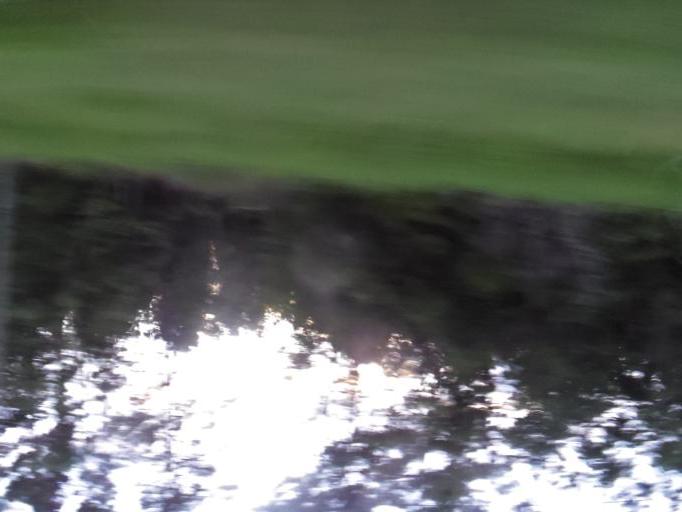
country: US
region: Georgia
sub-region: Camden County
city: Kingsland
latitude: 30.7706
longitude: -81.6870
